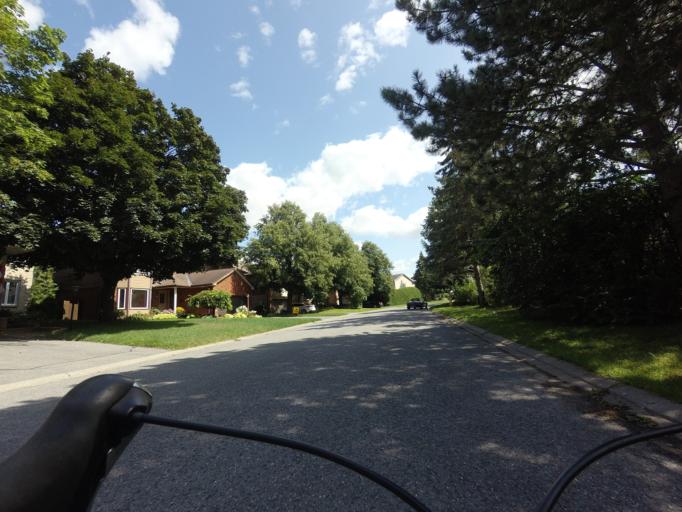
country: CA
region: Ontario
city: Bells Corners
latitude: 45.2915
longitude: -75.8658
